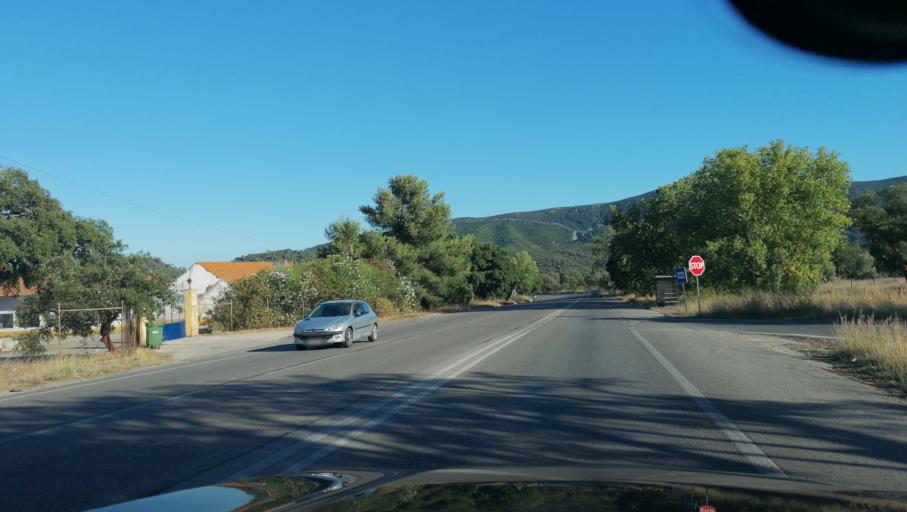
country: PT
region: Setubal
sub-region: Palmela
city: Quinta do Anjo
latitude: 38.5182
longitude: -8.9814
